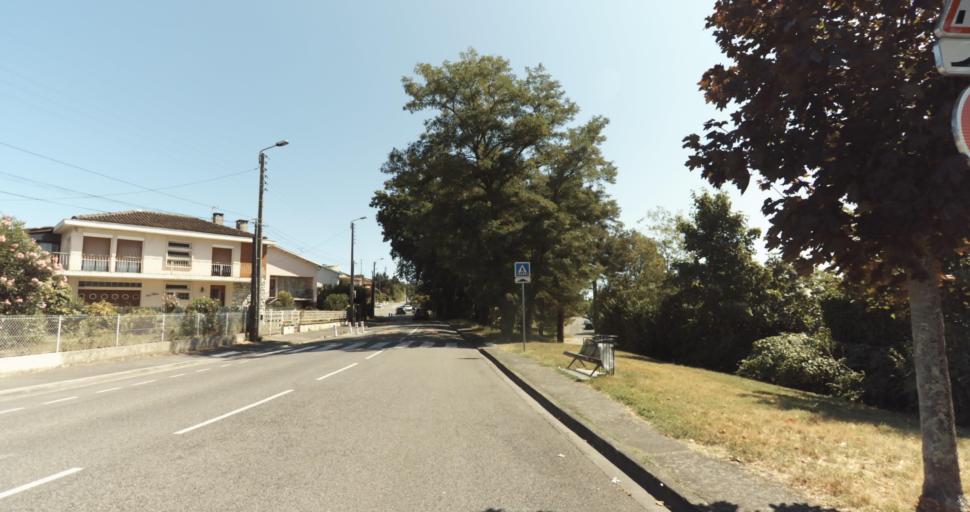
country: FR
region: Midi-Pyrenees
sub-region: Departement de la Haute-Garonne
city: L'Union
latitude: 43.6518
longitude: 1.4879
